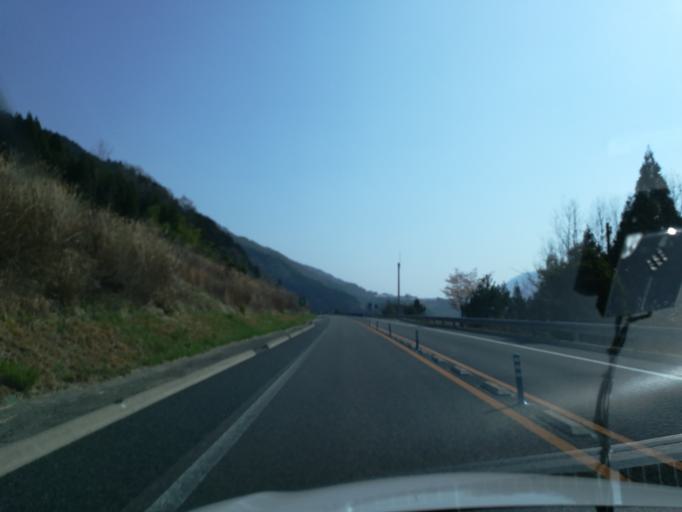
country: JP
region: Tokushima
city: Ikedacho
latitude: 34.0133
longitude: 133.7460
